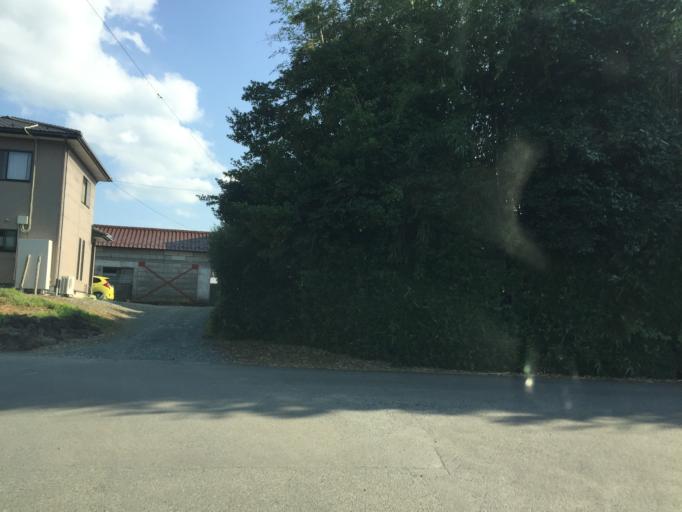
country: JP
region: Miyagi
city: Marumori
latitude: 37.8004
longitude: 140.8947
